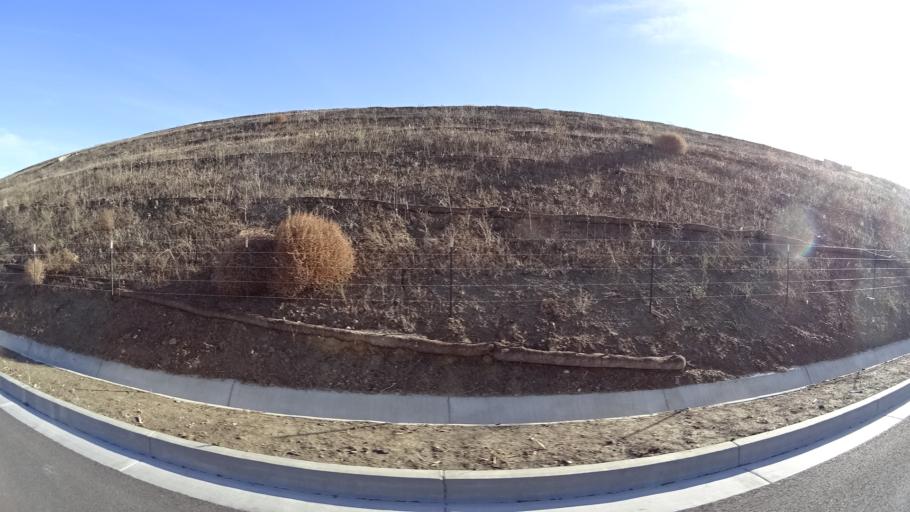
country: US
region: California
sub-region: Orange County
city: San Juan Capistrano
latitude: 33.5097
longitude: -117.6222
